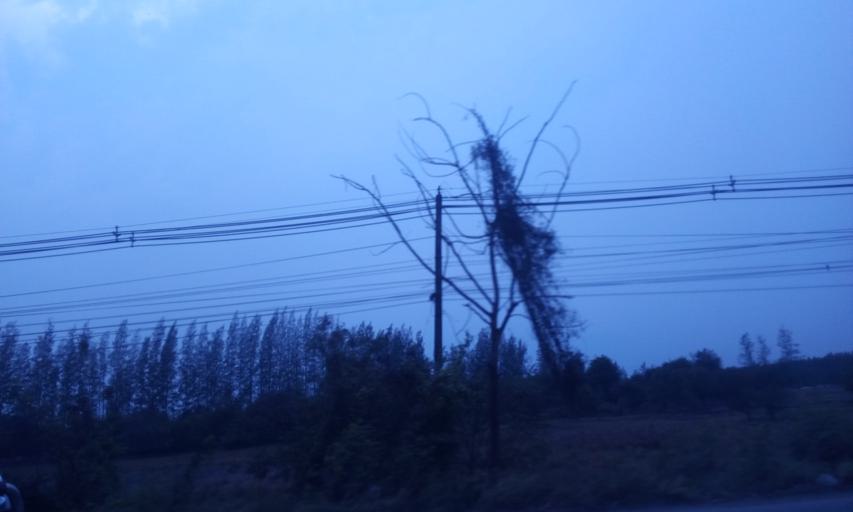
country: TH
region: Chon Buri
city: Ko Chan
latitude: 13.3028
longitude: 101.2627
